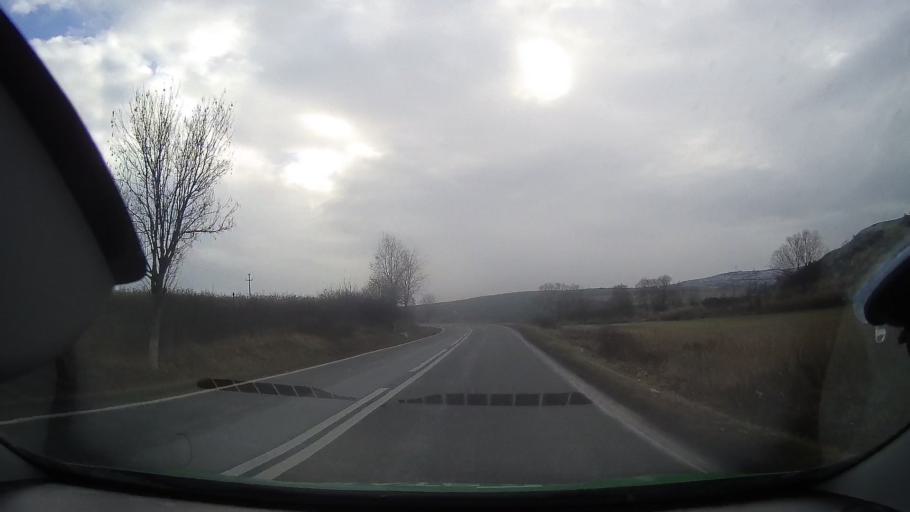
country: RO
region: Mures
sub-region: Comuna Cucerdea
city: Cucerdea
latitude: 46.3805
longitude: 24.2560
